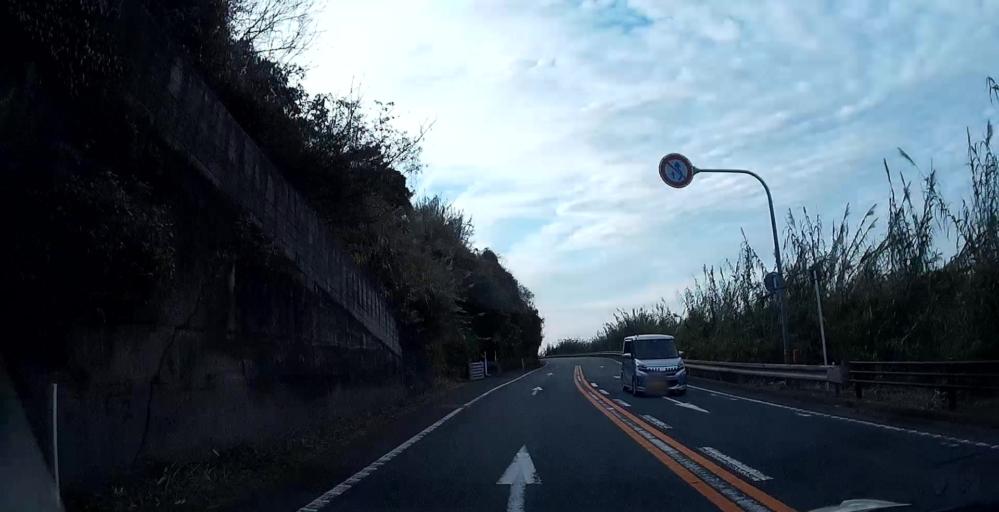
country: JP
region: Kumamoto
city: Matsubase
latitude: 32.6539
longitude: 130.5030
